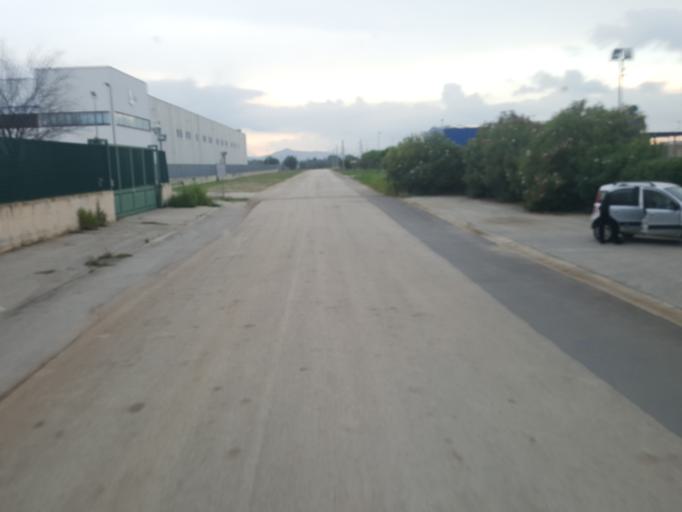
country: IT
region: Campania
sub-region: Provincia di Caserta
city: Pignataro Maggiore
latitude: 41.1760
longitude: 14.1426
